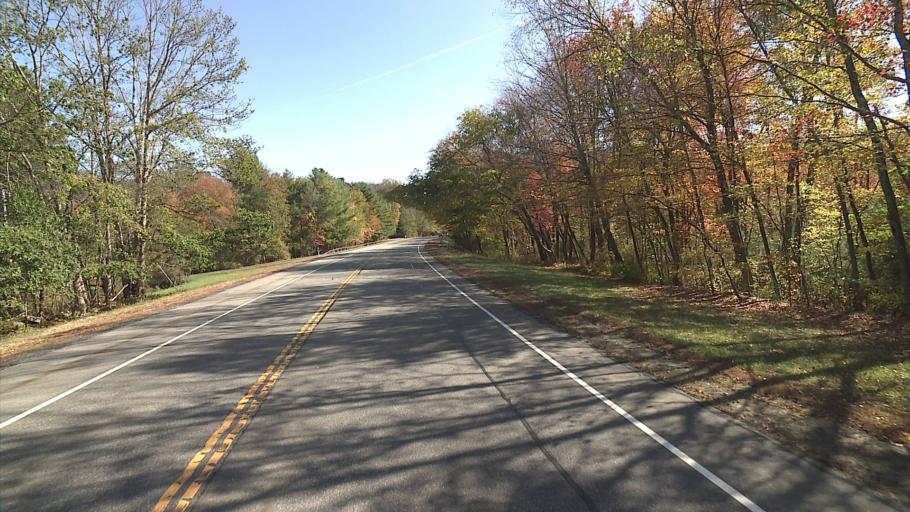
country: US
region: Connecticut
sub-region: Windham County
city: Wauregan
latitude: 41.7875
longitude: -72.0024
